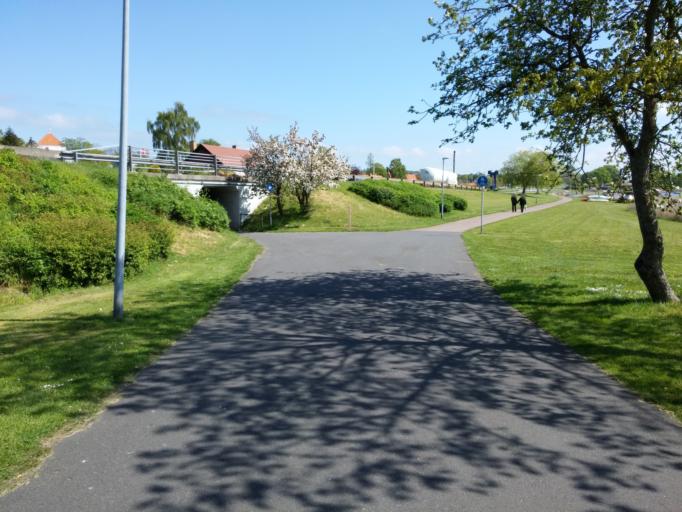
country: DK
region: South Denmark
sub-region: Kerteminde Kommune
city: Munkebo
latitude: 55.4542
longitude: 10.5532
